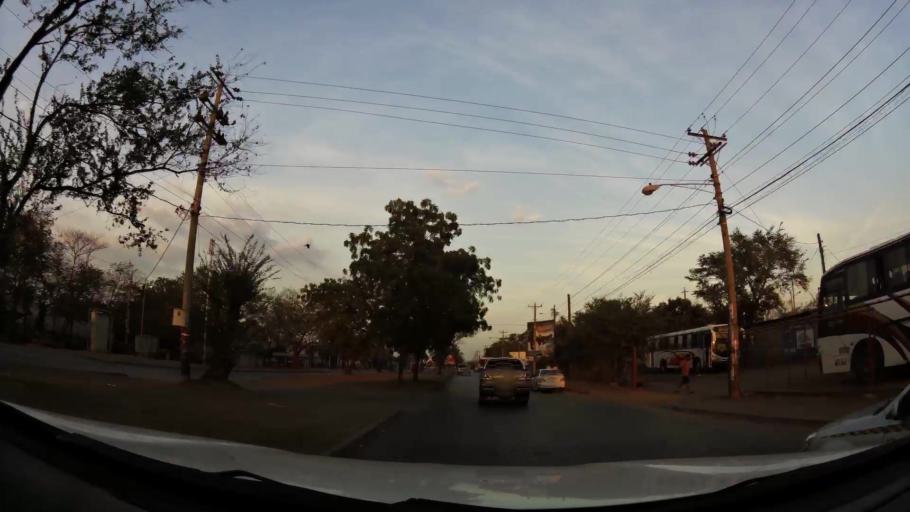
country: NI
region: Managua
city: Managua
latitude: 12.1337
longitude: -86.1966
